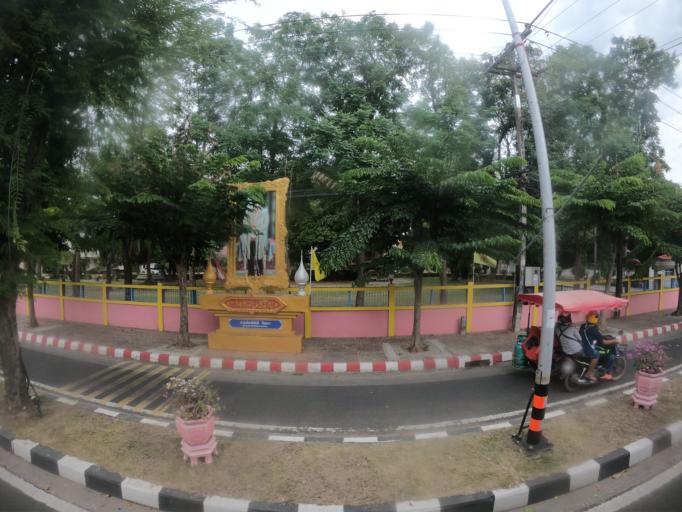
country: TH
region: Maha Sarakham
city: Maha Sarakham
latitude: 16.1863
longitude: 103.3011
